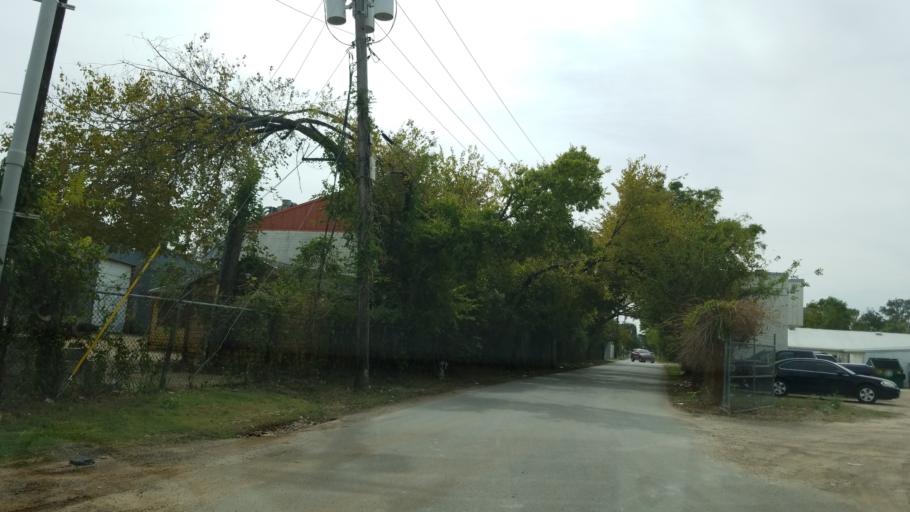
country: US
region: Texas
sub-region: Dallas County
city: Dallas
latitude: 32.7662
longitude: -96.7383
